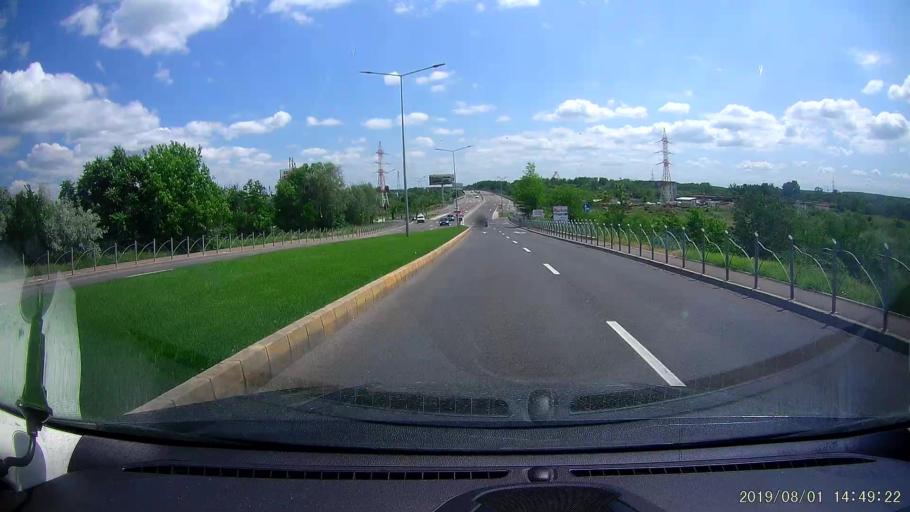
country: RO
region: Galati
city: Galati
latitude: 45.4059
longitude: 28.0151
